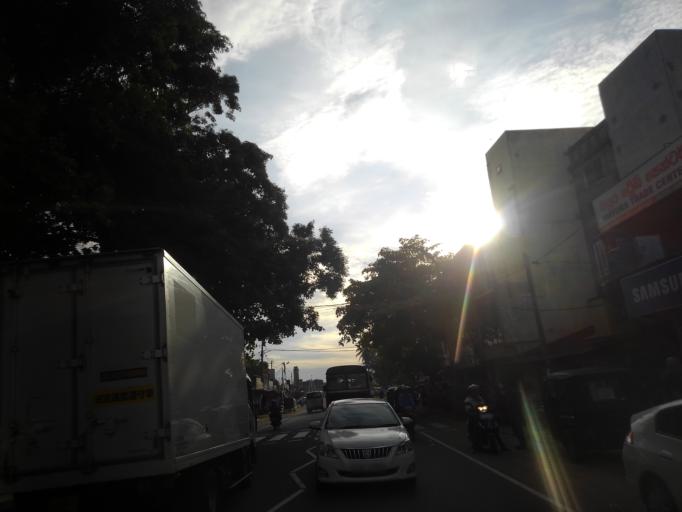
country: LK
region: Southern
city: Galle
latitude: 6.0337
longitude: 80.2184
